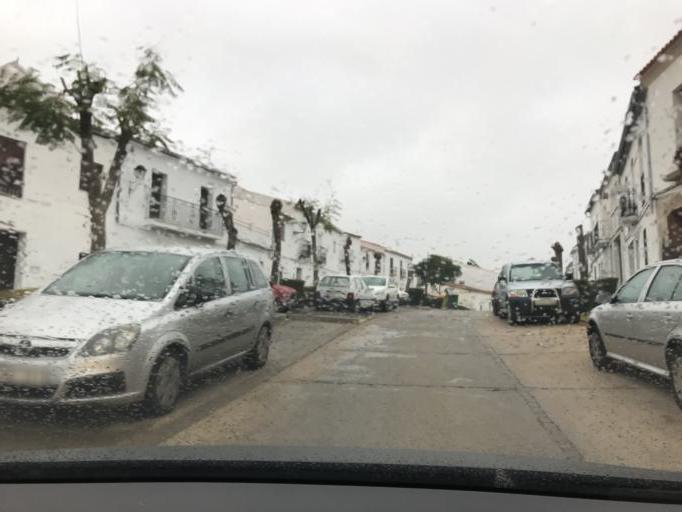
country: ES
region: Andalusia
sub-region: Provincia de Sevilla
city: Guadalcanal
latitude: 38.0957
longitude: -5.8175
